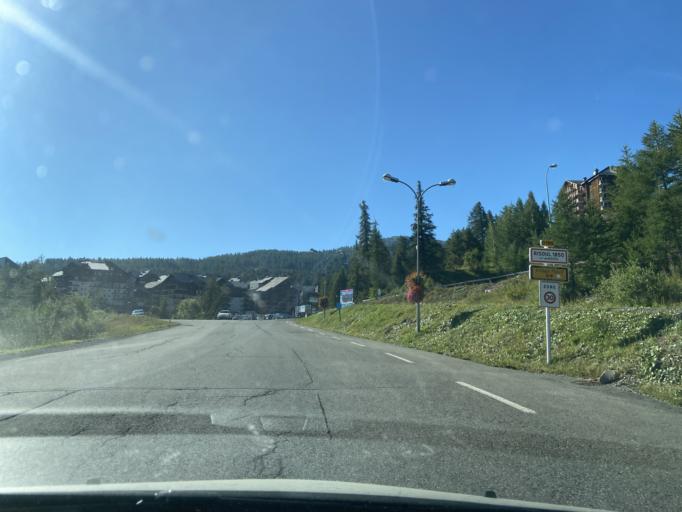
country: FR
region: Provence-Alpes-Cote d'Azur
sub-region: Departement des Hautes-Alpes
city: Guillestre
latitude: 44.6243
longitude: 6.6309
